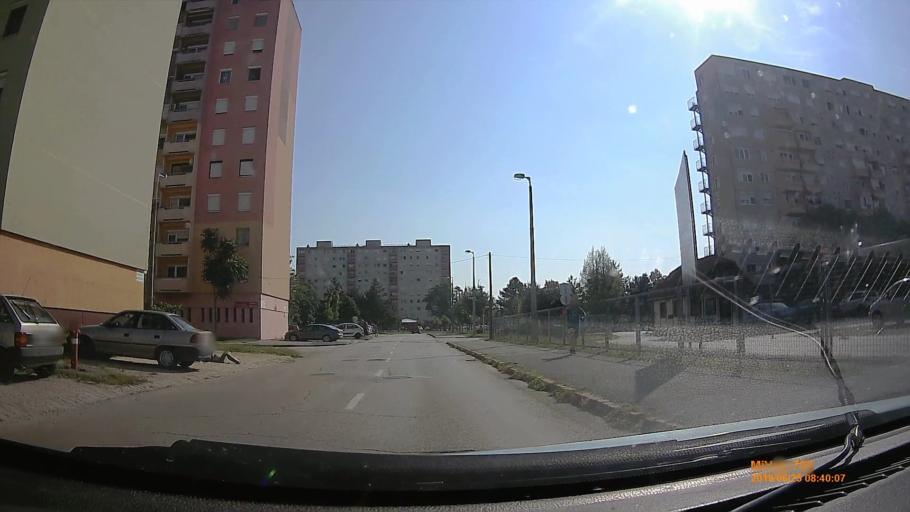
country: HU
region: Fejer
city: Szekesfehervar
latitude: 47.1878
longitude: 18.4015
